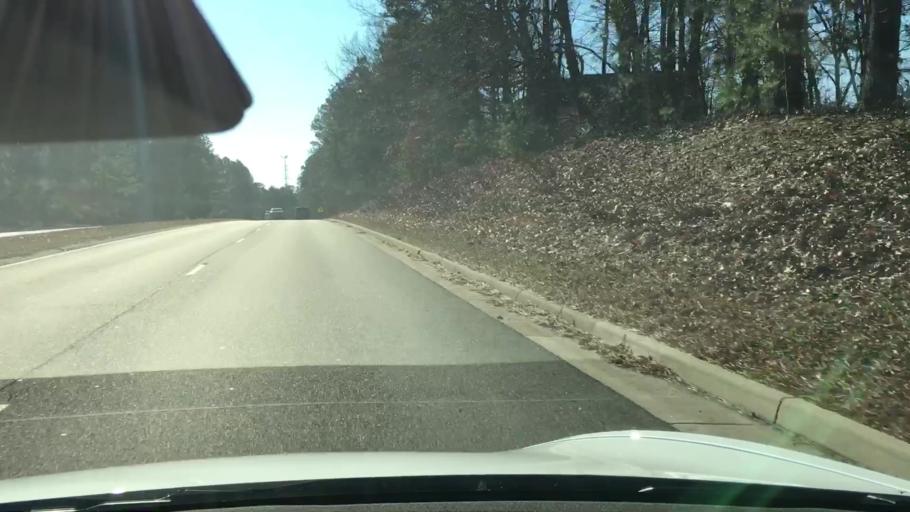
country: US
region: Virginia
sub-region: Henrico County
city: Tuckahoe
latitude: 37.5861
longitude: -77.5714
